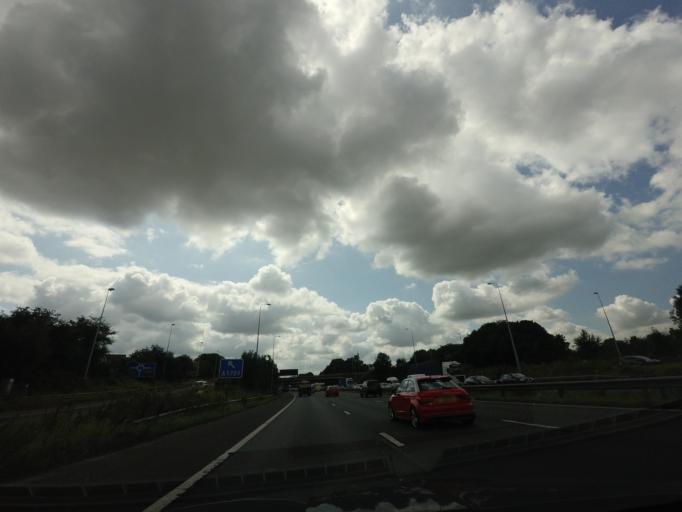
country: GB
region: England
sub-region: Borough of Wigan
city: Shevington
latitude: 53.5918
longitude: -2.6941
